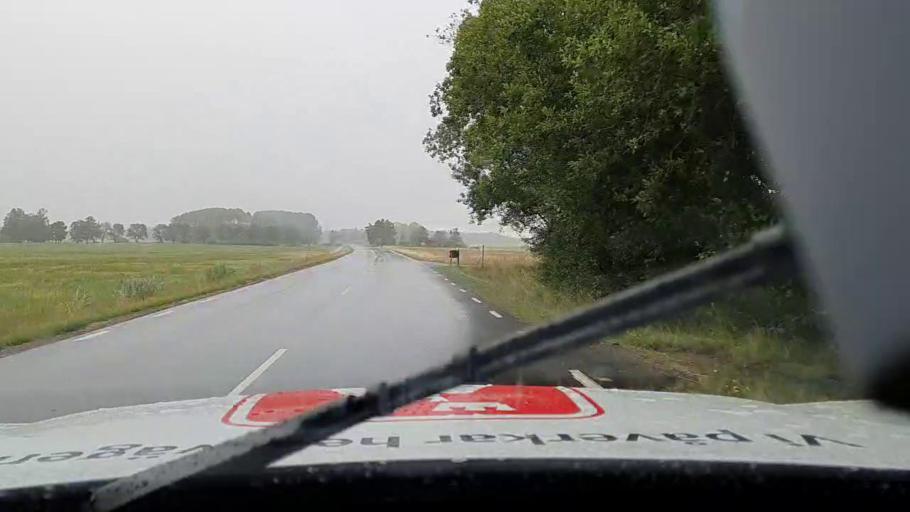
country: SE
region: Vaestra Goetaland
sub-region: Toreboda Kommun
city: Toereboda
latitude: 58.6691
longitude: 14.1323
